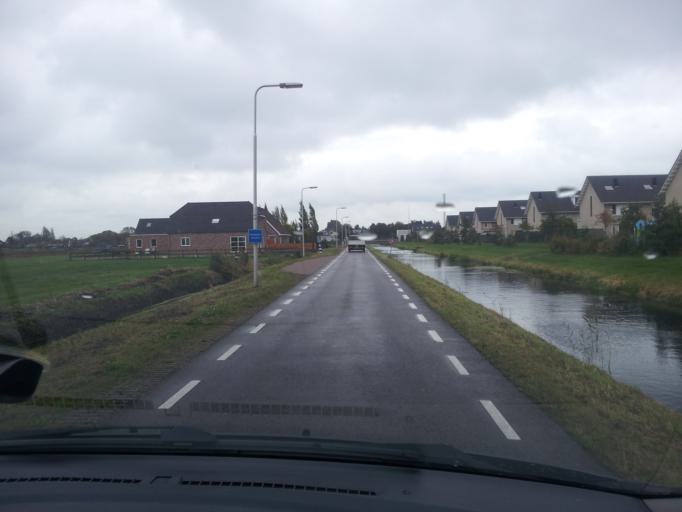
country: NL
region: South Holland
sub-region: Gemeente Lansingerland
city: Berkel en Rodenrijs
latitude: 52.0052
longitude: 4.4766
